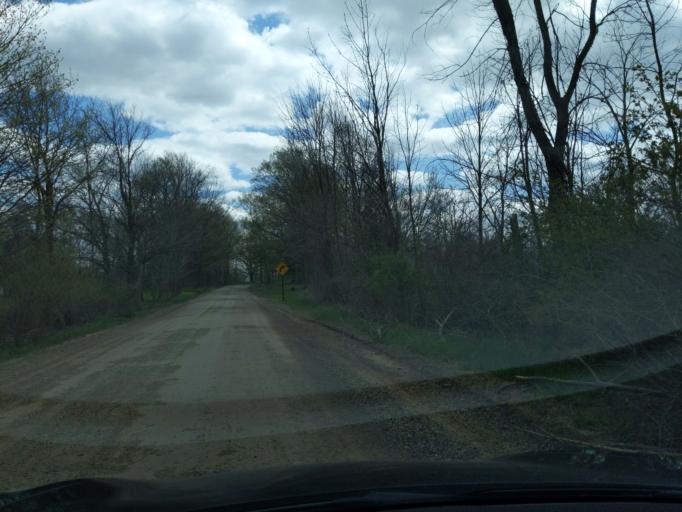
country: US
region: Michigan
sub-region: Eaton County
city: Dimondale
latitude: 42.6382
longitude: -84.6127
